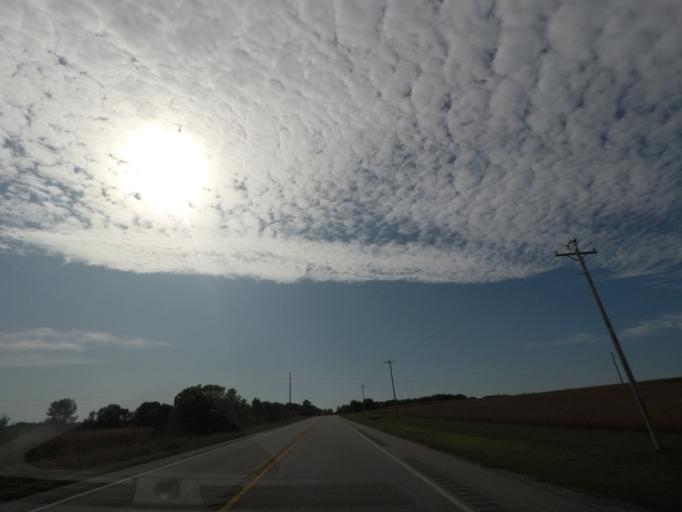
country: US
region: Iowa
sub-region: Story County
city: Gilbert
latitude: 42.0872
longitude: -93.6203
